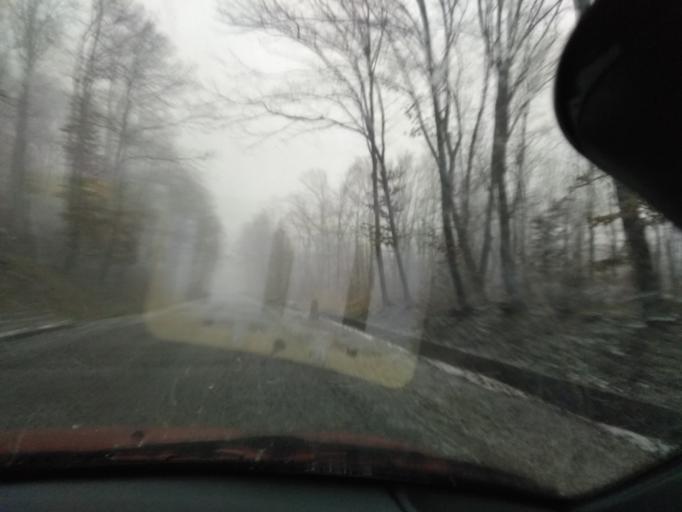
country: AT
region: Lower Austria
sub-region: Politischer Bezirk Wien-Umgebung
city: Klosterneuburg
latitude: 48.2559
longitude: 16.2777
